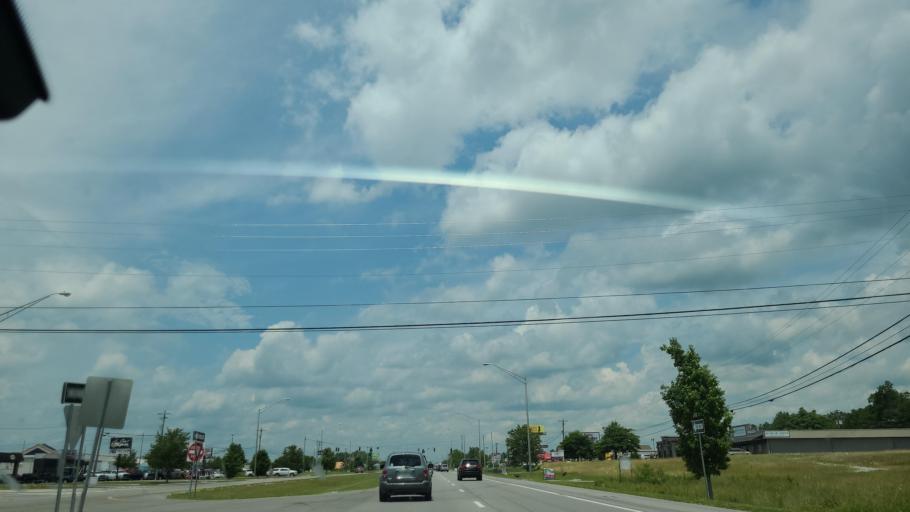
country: US
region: Tennessee
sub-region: Cumberland County
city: Crossville
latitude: 35.9770
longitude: -85.0383
